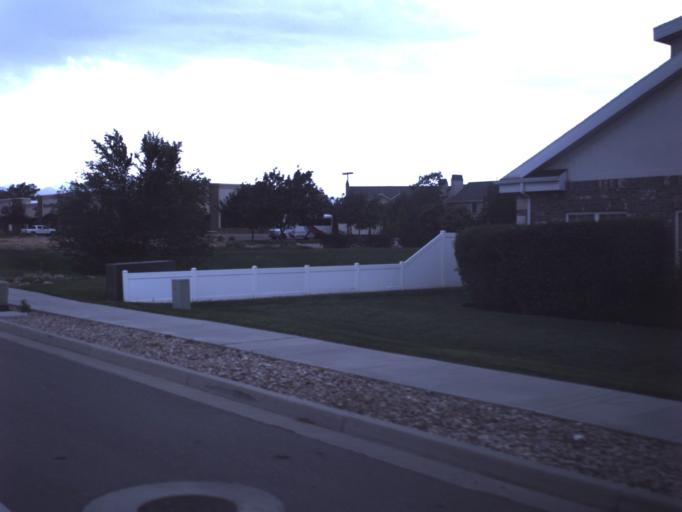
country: US
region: Utah
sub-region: Salt Lake County
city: Riverton
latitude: 40.5224
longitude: -111.9512
